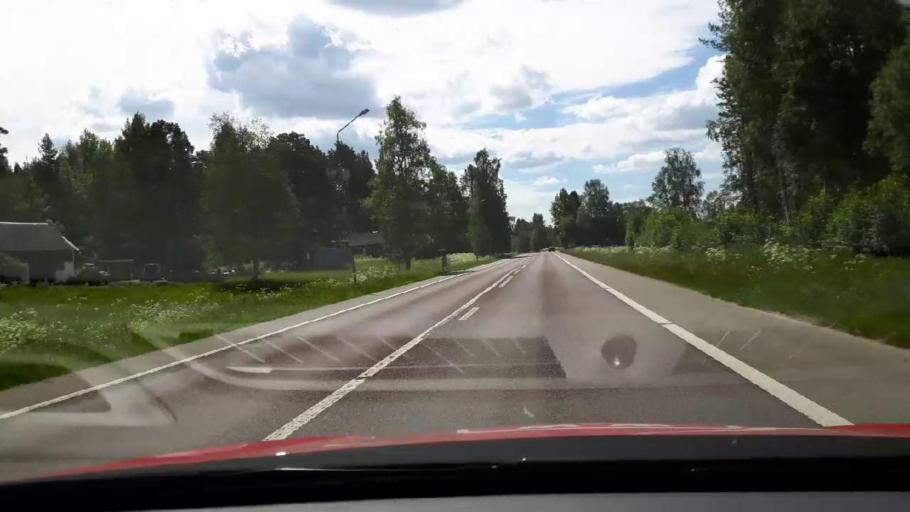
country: SE
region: Jaemtland
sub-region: Harjedalens Kommun
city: Sveg
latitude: 62.1693
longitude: 14.9512
